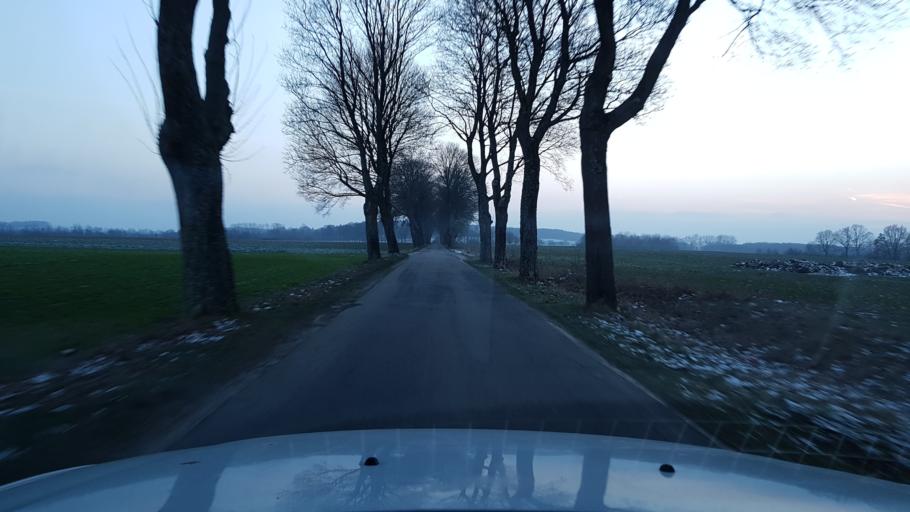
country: PL
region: West Pomeranian Voivodeship
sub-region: Powiat bialogardzki
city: Karlino
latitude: 54.0012
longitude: 15.8295
